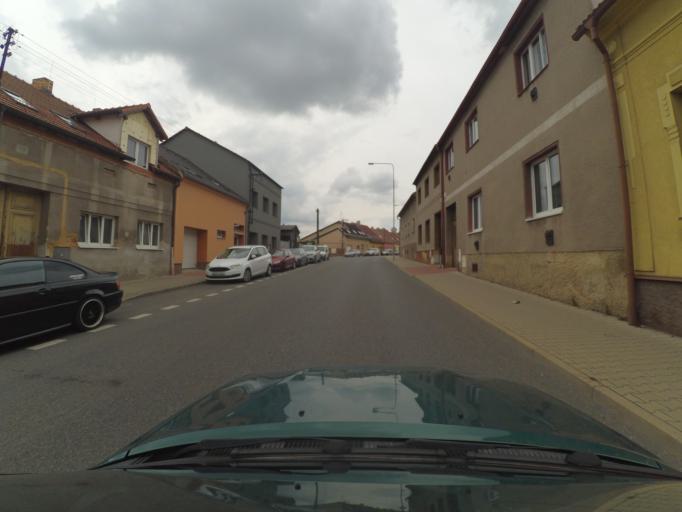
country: CZ
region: Central Bohemia
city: Rakovnik
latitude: 50.1035
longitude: 13.7372
